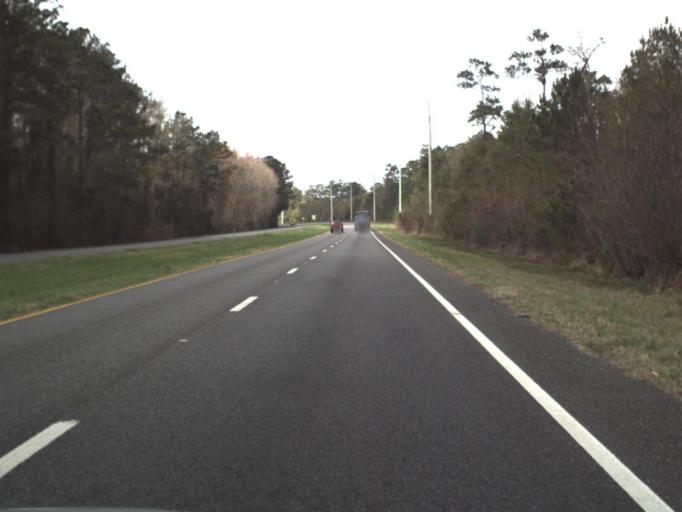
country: US
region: Florida
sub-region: Leon County
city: Woodville
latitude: 30.4109
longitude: -84.0699
